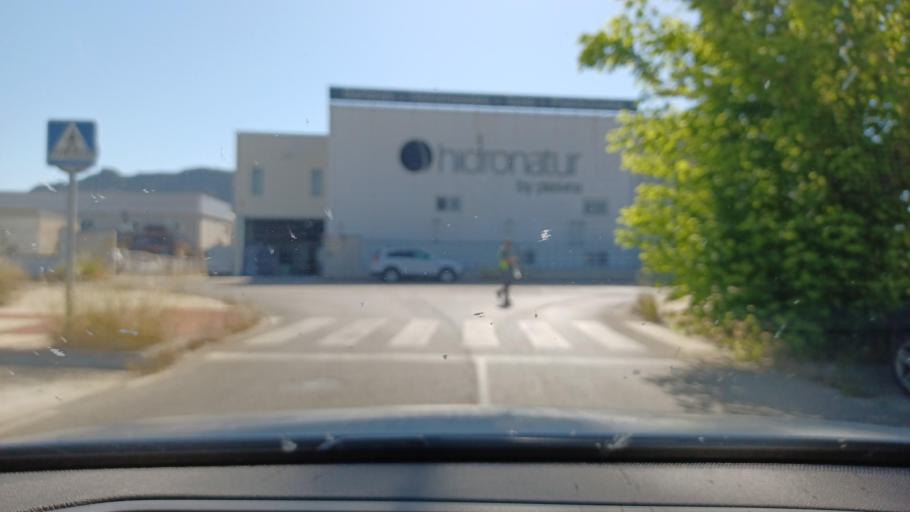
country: ES
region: Valencia
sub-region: Provincia de Valencia
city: Xativa
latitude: 38.9977
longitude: -0.5082
